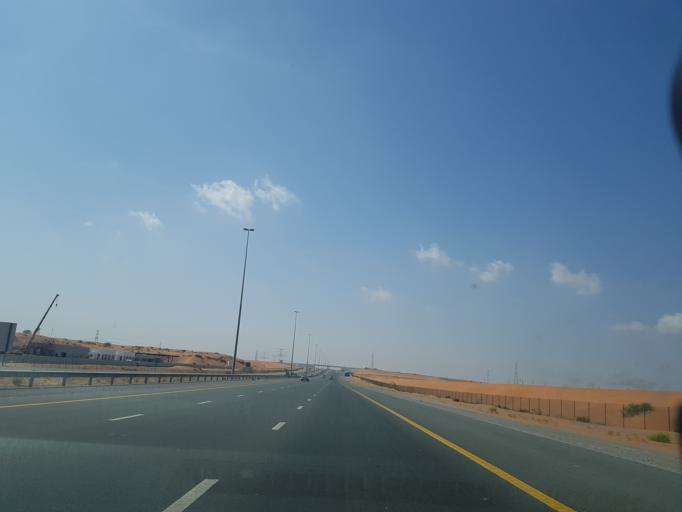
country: AE
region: Ra's al Khaymah
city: Ras al-Khaimah
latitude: 25.7034
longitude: 55.9352
